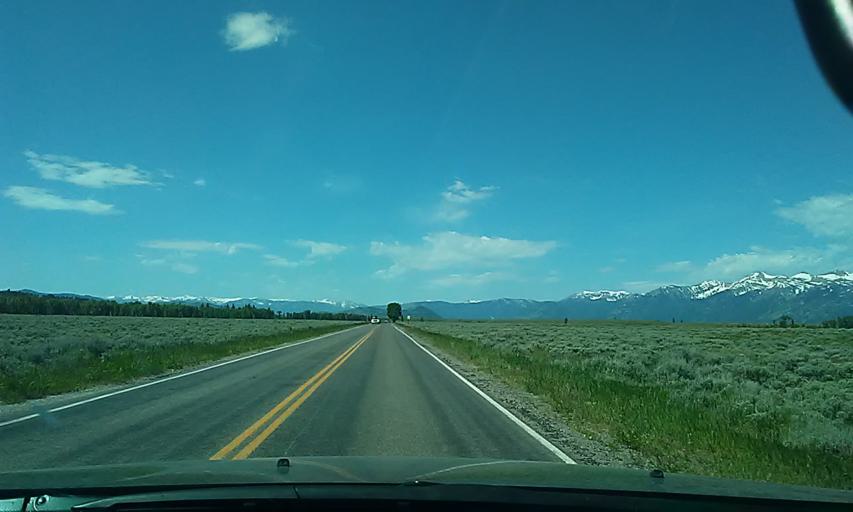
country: US
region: Wyoming
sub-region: Teton County
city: Jackson
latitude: 43.6202
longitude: -110.6706
